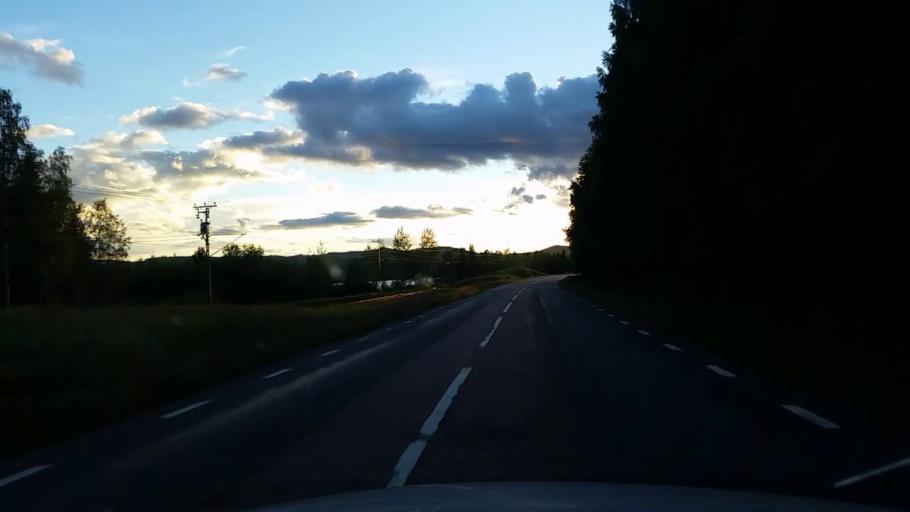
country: SE
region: Gaevleborg
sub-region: Ljusdals Kommun
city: Farila
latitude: 62.1303
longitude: 15.7020
